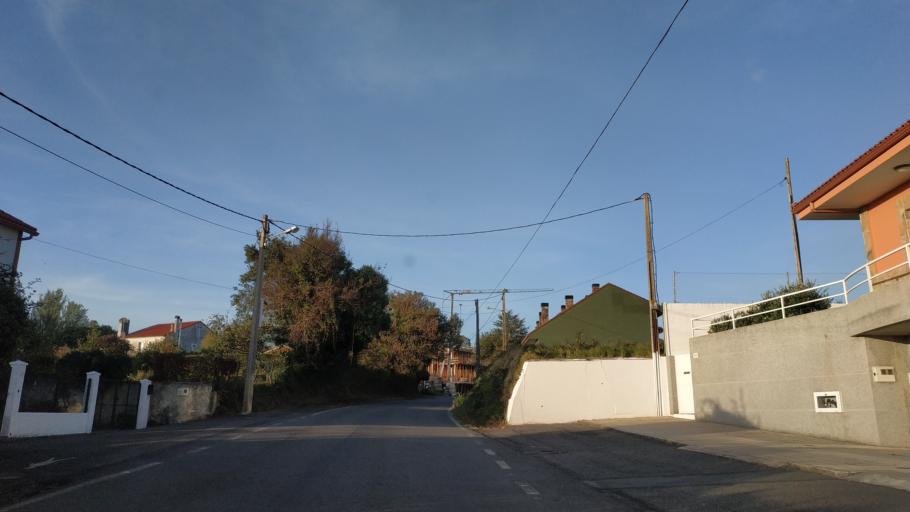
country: ES
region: Galicia
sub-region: Provincia da Coruna
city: Oleiros
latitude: 43.3621
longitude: -8.3416
